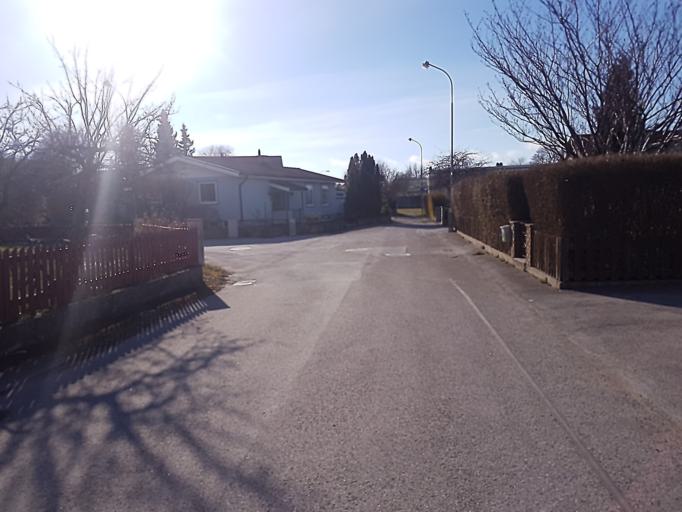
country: SE
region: Gotland
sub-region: Gotland
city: Visby
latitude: 57.6207
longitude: 18.2931
